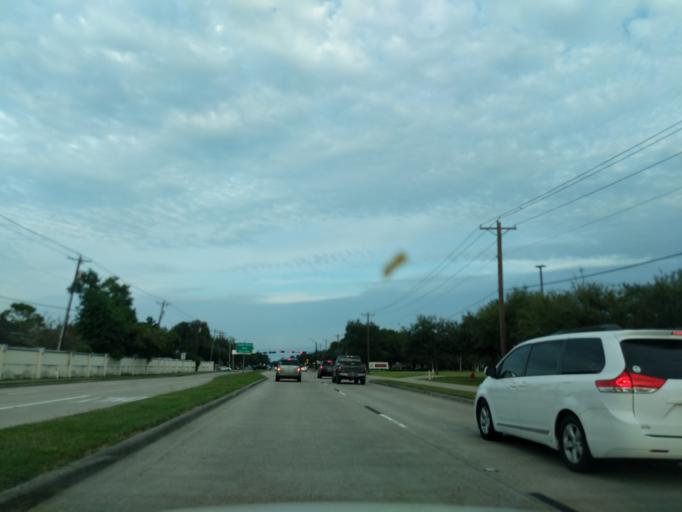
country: US
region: Texas
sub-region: Galveston County
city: Clear Lake Shores
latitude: 29.5260
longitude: -95.0501
